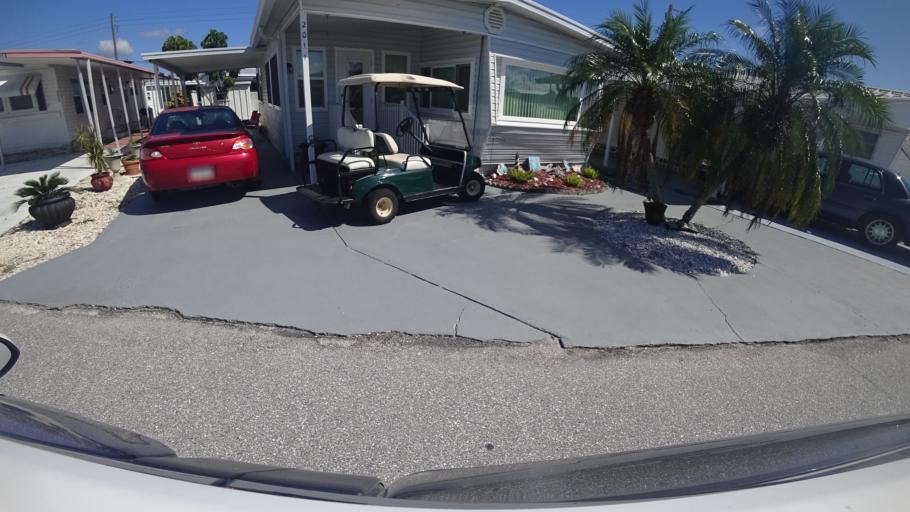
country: US
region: Florida
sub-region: Manatee County
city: Bayshore Gardens
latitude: 27.4219
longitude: -82.5821
